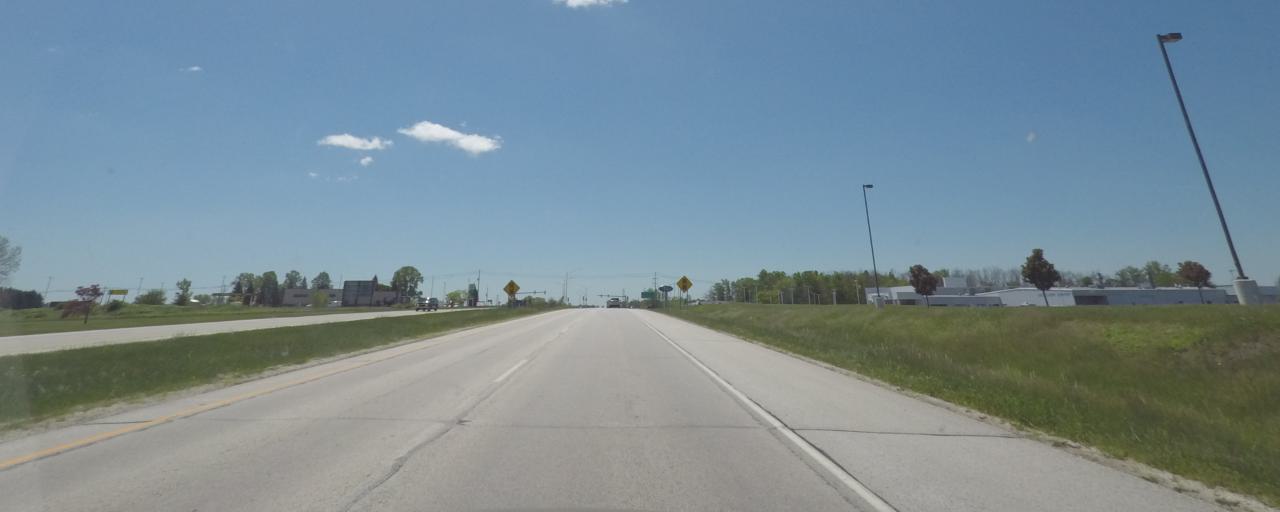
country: US
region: Wisconsin
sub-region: Sheboygan County
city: Plymouth
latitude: 43.7355
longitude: -87.9413
